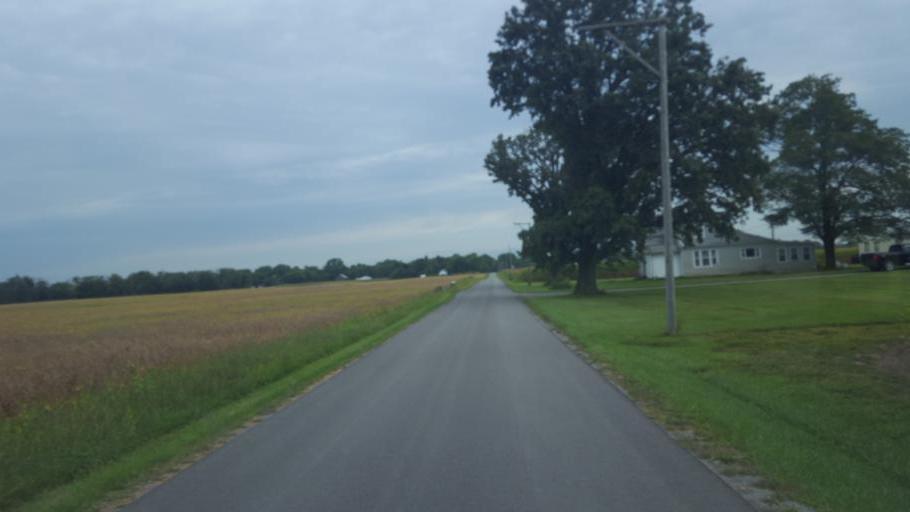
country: US
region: Ohio
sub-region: Wyandot County
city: Upper Sandusky
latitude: 40.7508
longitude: -83.1883
